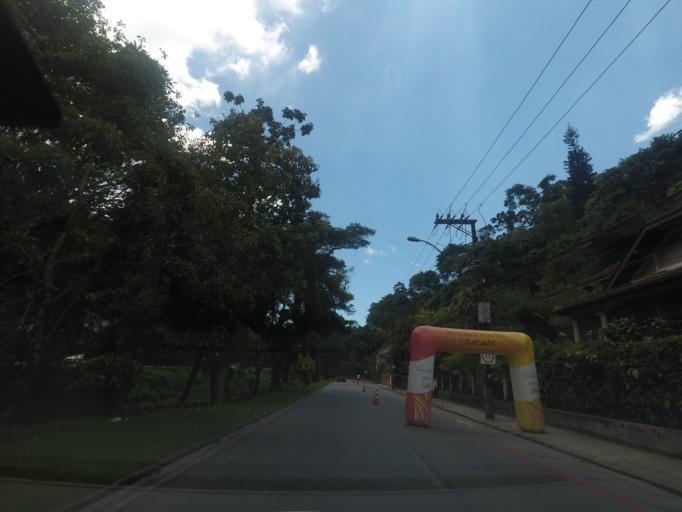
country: BR
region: Rio de Janeiro
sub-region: Petropolis
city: Petropolis
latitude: -22.5029
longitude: -43.1818
